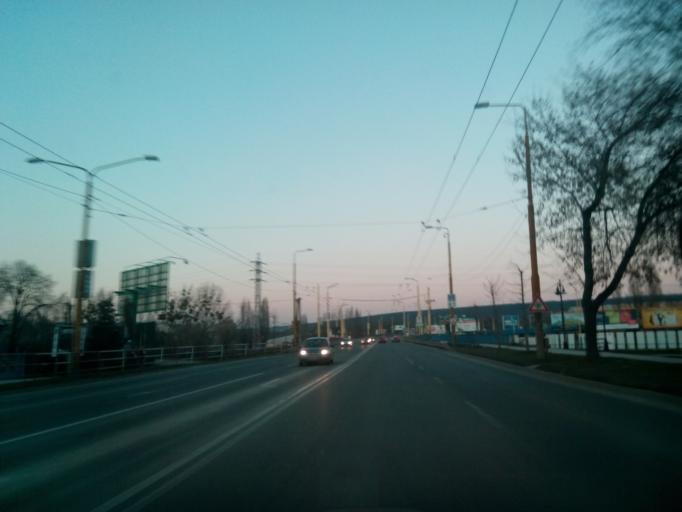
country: SK
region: Kosicky
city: Kosice
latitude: 48.7406
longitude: 21.2564
